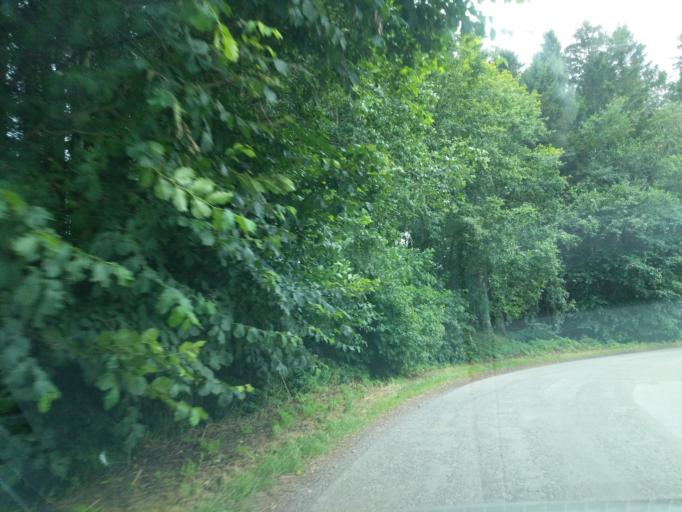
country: GB
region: Scotland
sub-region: Moray
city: Rothes
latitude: 57.4761
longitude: -3.1939
